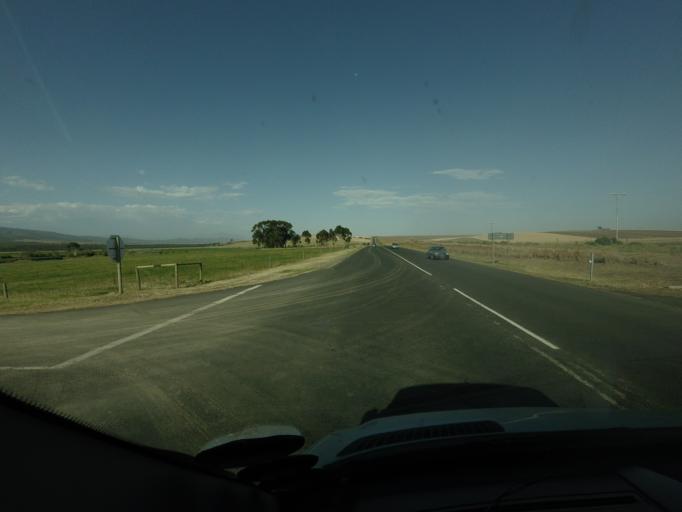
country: ZA
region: Western Cape
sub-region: Cape Winelands District Municipality
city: Ashton
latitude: -34.1427
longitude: 19.9943
